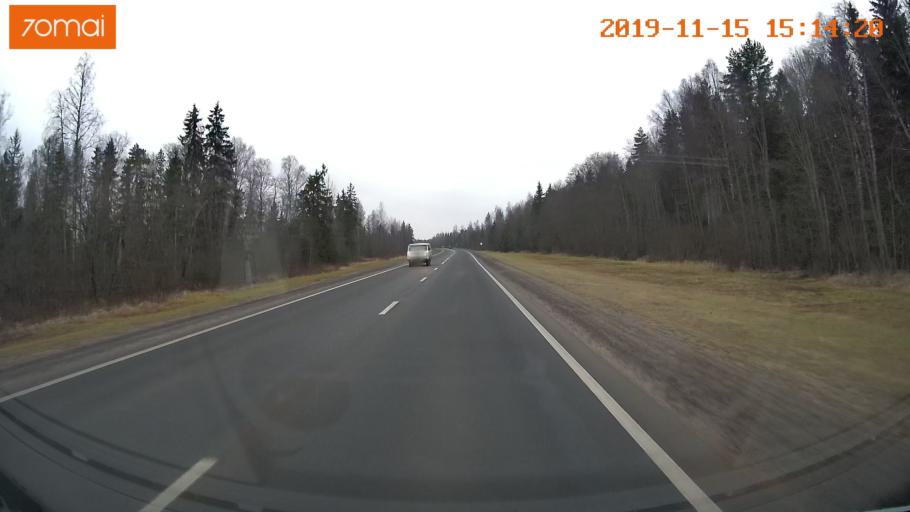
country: RU
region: Jaroslavl
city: Danilov
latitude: 58.3012
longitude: 40.2065
